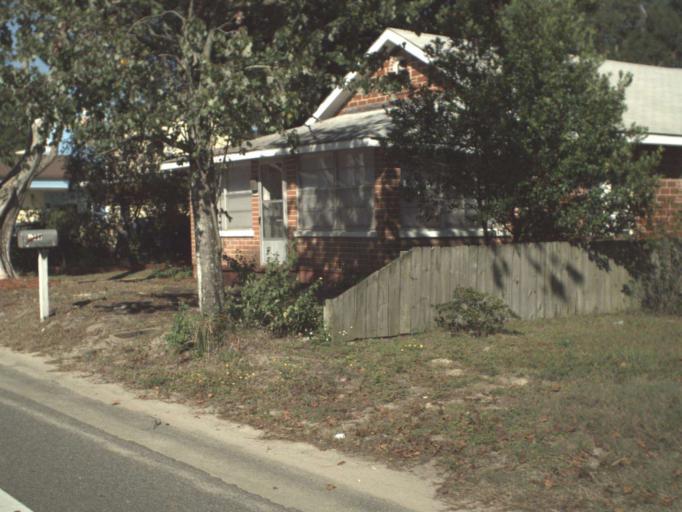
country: US
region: Florida
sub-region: Bay County
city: Pretty Bayou
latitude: 30.1798
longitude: -85.7014
